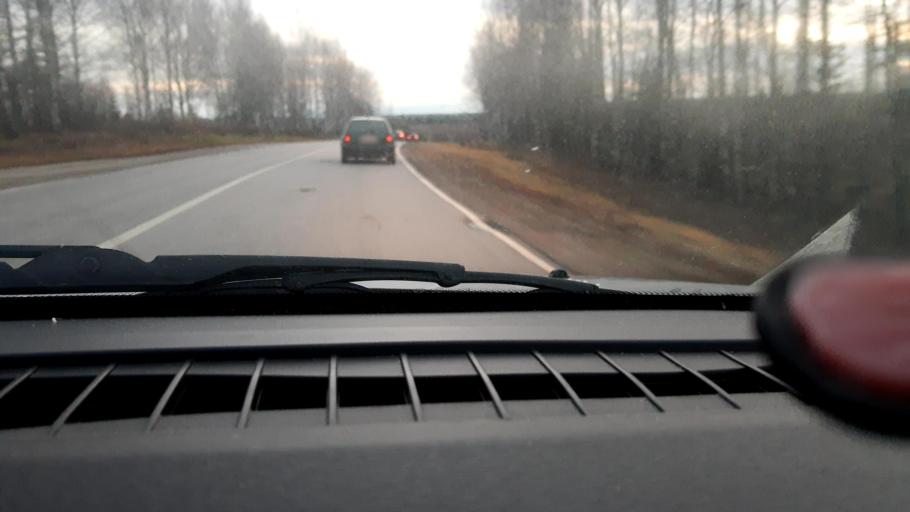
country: RU
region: Nizjnij Novgorod
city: Krasnyye Baki
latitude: 57.0484
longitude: 45.1352
